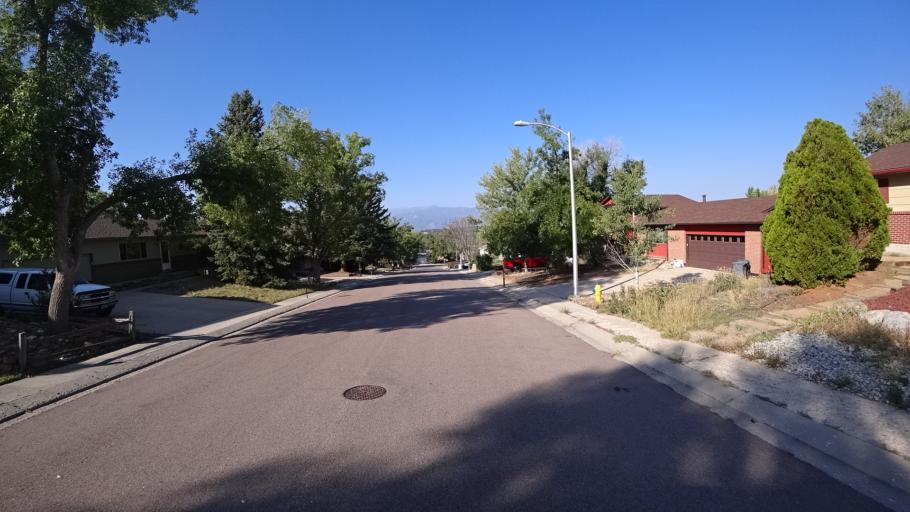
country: US
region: Colorado
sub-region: El Paso County
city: Cimarron Hills
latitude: 38.8807
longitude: -104.7350
